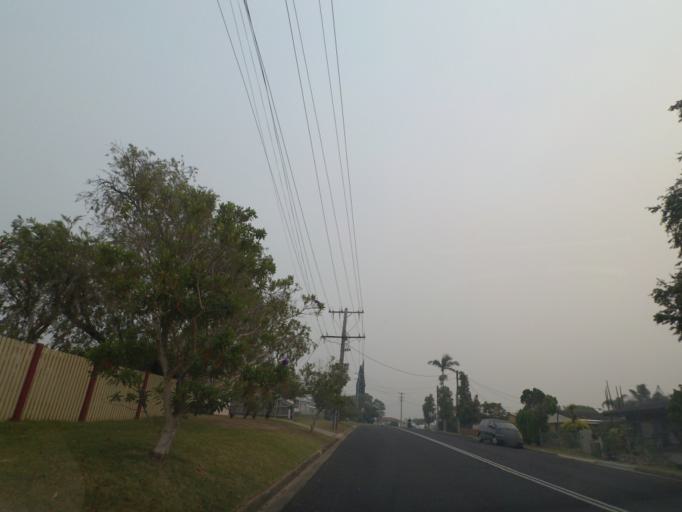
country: AU
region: New South Wales
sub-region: Coffs Harbour
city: Coffs Harbour
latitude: -30.2900
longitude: 153.1076
